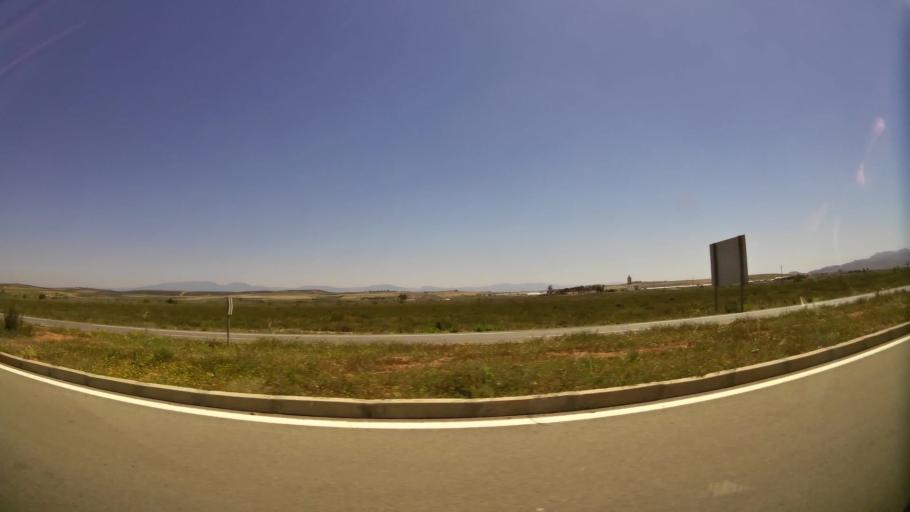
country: MA
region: Oriental
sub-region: Berkane-Taourirt
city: Madagh
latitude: 35.1053
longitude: -2.3476
